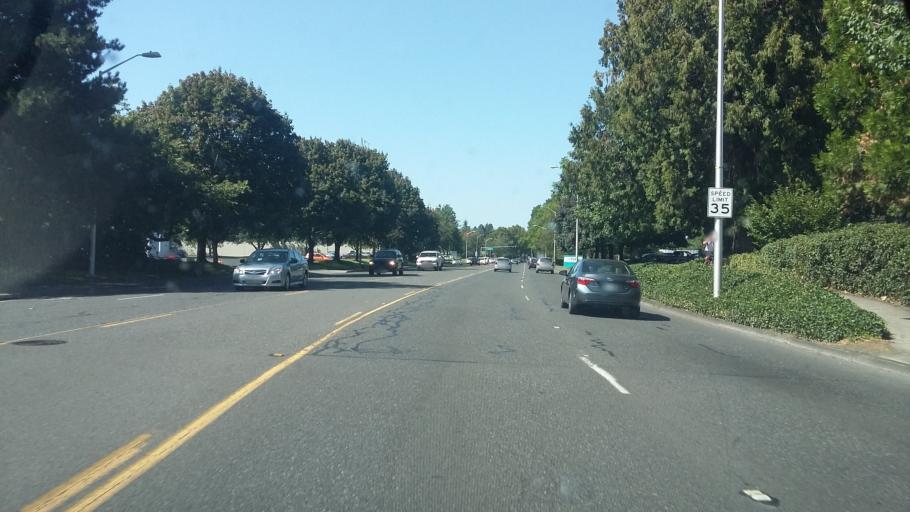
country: US
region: Washington
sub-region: Clark County
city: Orchards
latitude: 45.6470
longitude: -122.5582
